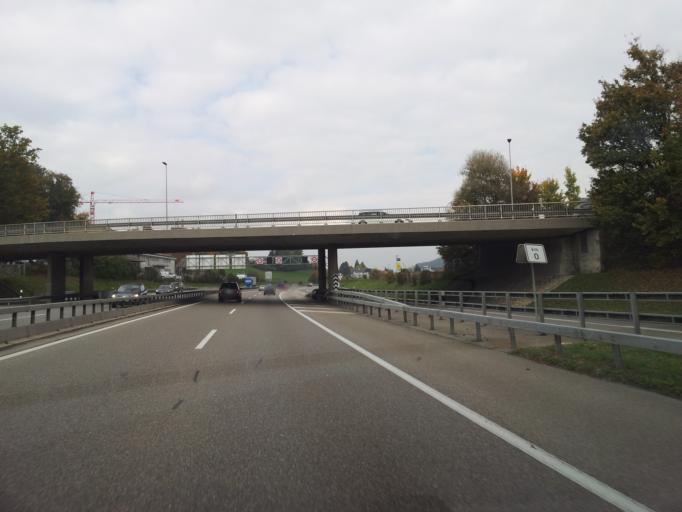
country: CH
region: Bern
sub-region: Bern-Mittelland District
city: Muri
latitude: 46.9250
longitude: 7.5032
